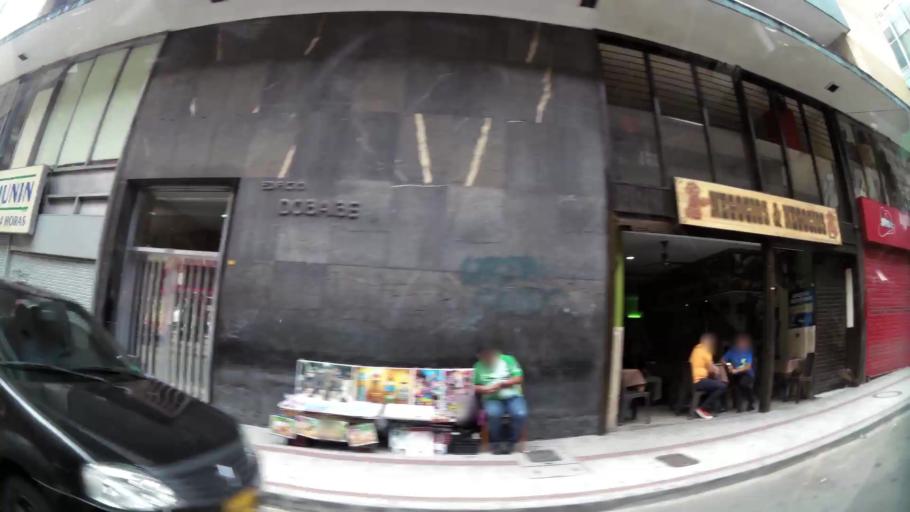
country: CO
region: Antioquia
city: Medellin
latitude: 6.2493
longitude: -75.5658
